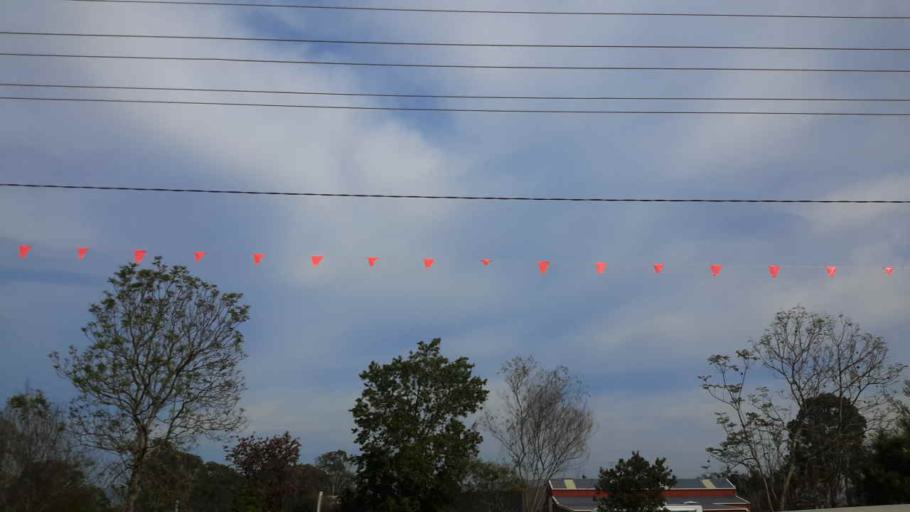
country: AU
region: New South Wales
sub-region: Penrith Municipality
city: Kingswood Park
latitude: -33.7873
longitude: 150.7020
